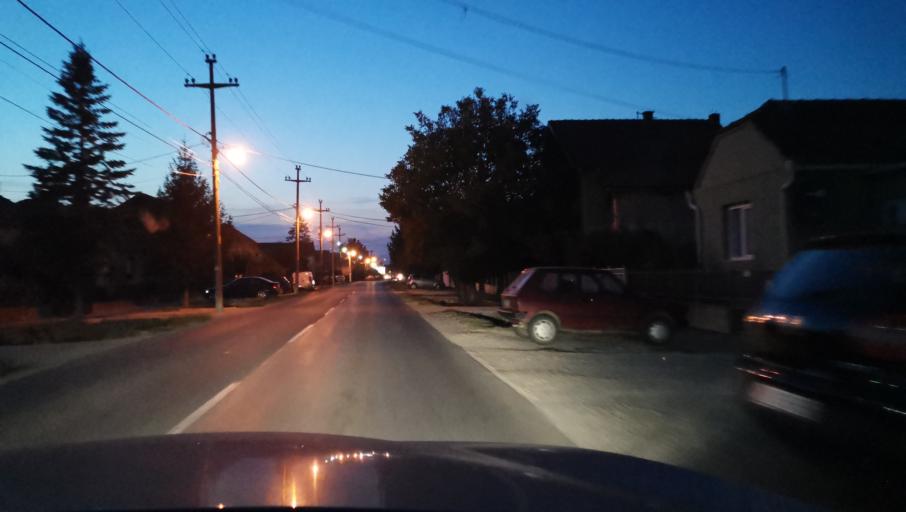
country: RS
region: Central Serbia
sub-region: Belgrade
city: Surcin
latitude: 44.7572
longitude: 20.2572
